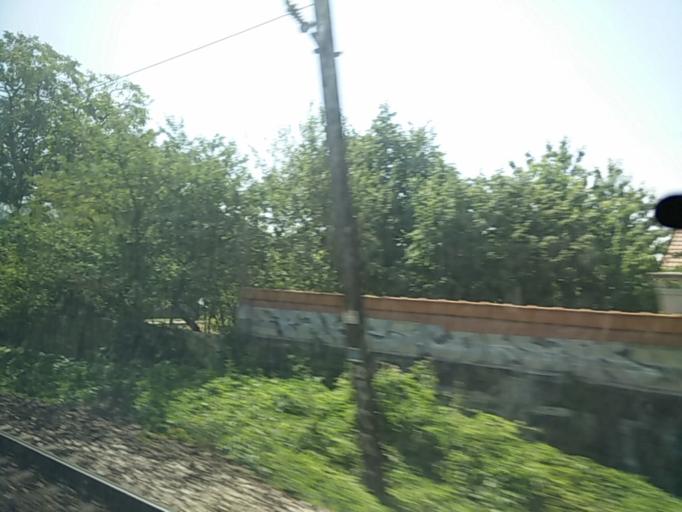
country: FR
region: Ile-de-France
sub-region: Departement du Val-de-Marne
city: Bry-sur-Marne
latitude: 48.8244
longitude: 2.5174
